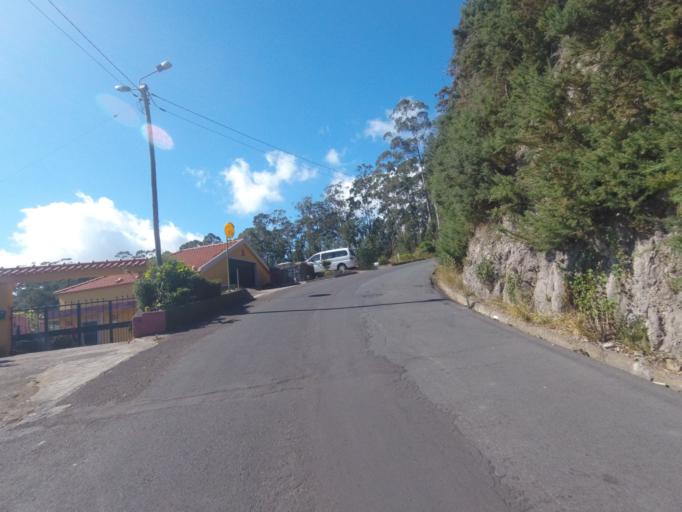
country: PT
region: Madeira
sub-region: Ribeira Brava
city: Campanario
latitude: 32.6865
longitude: -17.0219
